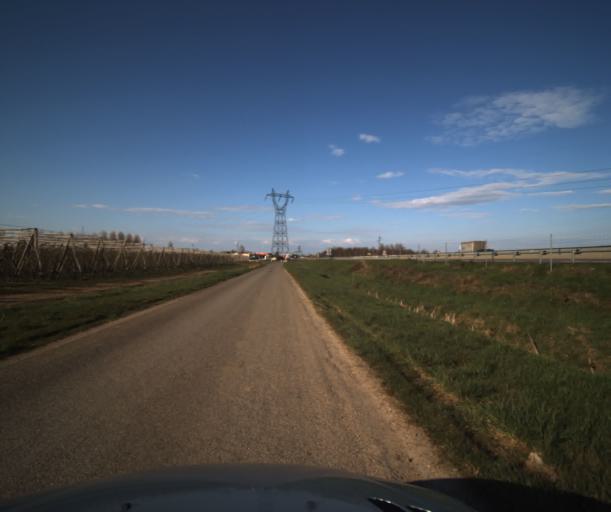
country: FR
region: Midi-Pyrenees
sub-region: Departement du Tarn-et-Garonne
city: Bressols
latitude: 43.9550
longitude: 1.3264
